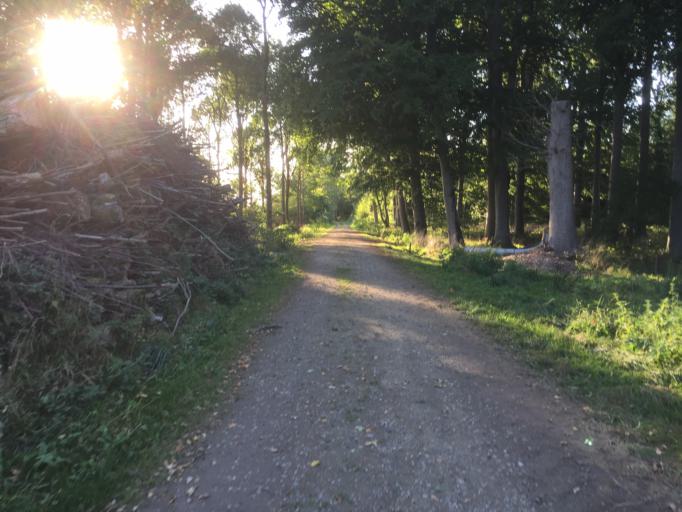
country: DK
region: South Denmark
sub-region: Odense Kommune
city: Hojby
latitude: 55.3552
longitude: 10.4372
